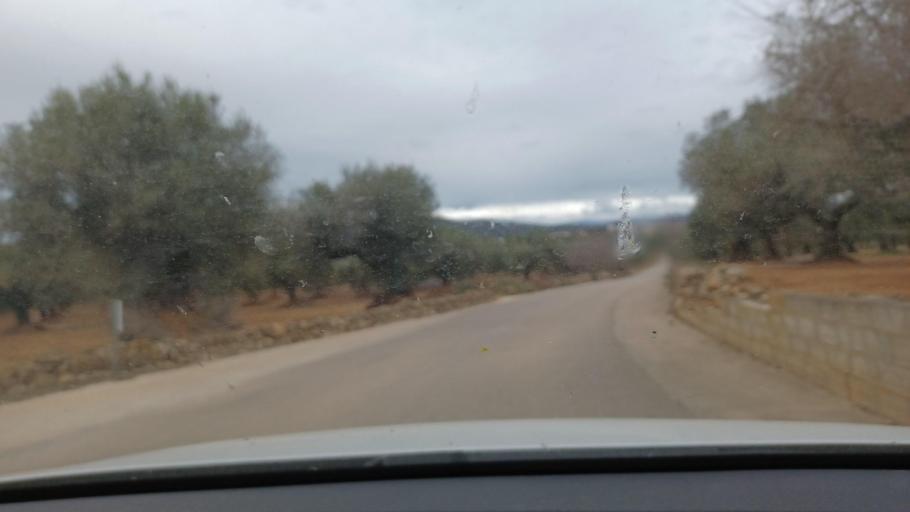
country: ES
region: Valencia
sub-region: Provincia de Castello
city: Traiguera
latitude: 40.5115
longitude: 0.2931
